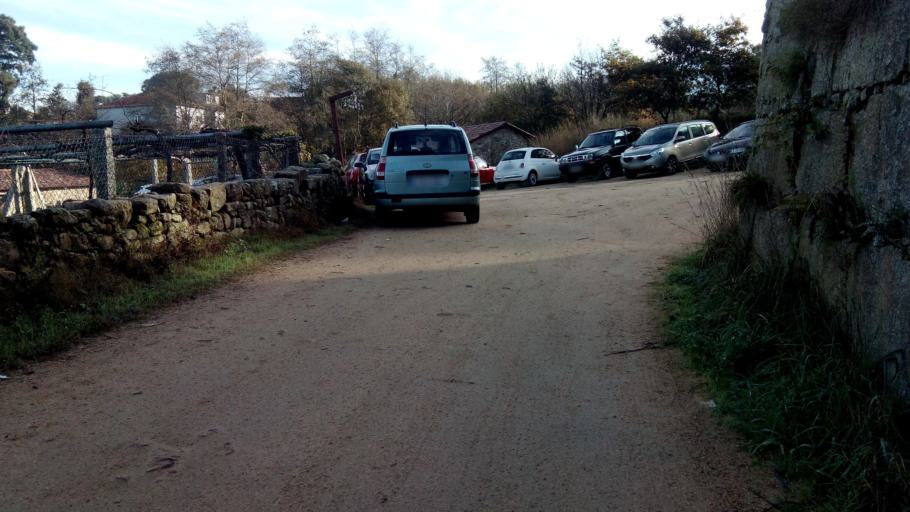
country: ES
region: Galicia
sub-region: Provincia de Pontevedra
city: Meis
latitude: 42.4920
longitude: -8.7581
